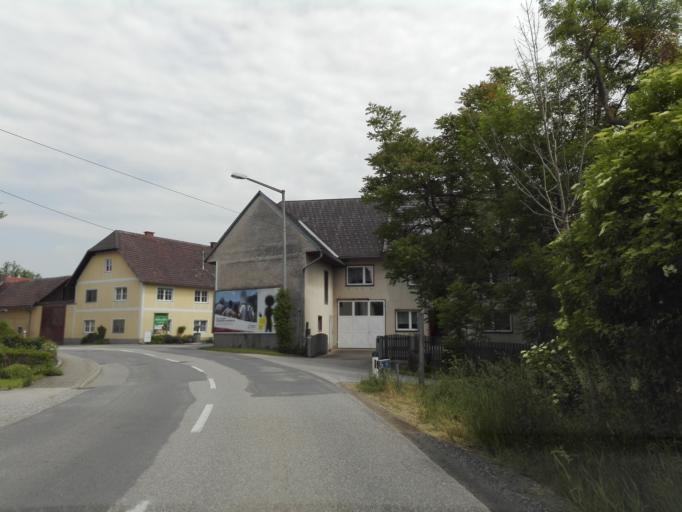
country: AT
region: Upper Austria
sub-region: Politischer Bezirk Urfahr-Umgebung
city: Feldkirchen an der Donau
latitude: 48.3507
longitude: 13.9959
